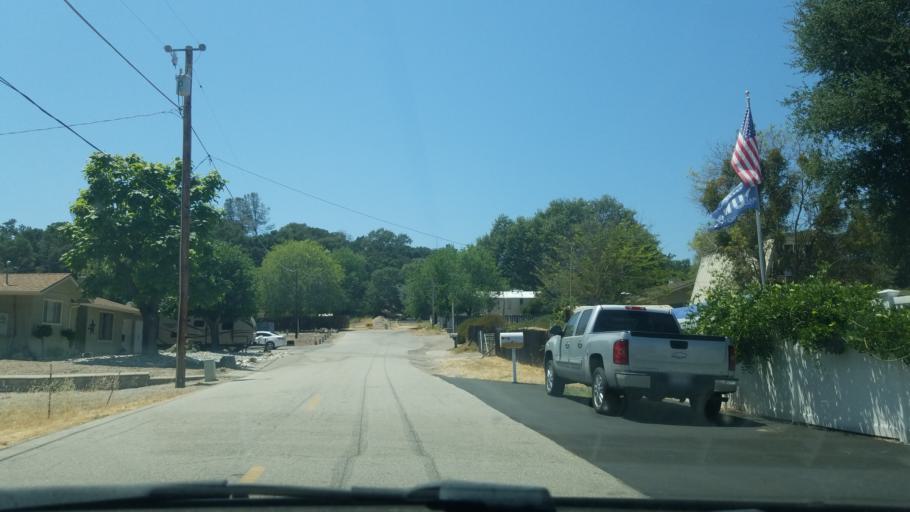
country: US
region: California
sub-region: San Luis Obispo County
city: Atascadero
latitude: 35.5085
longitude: -120.6665
